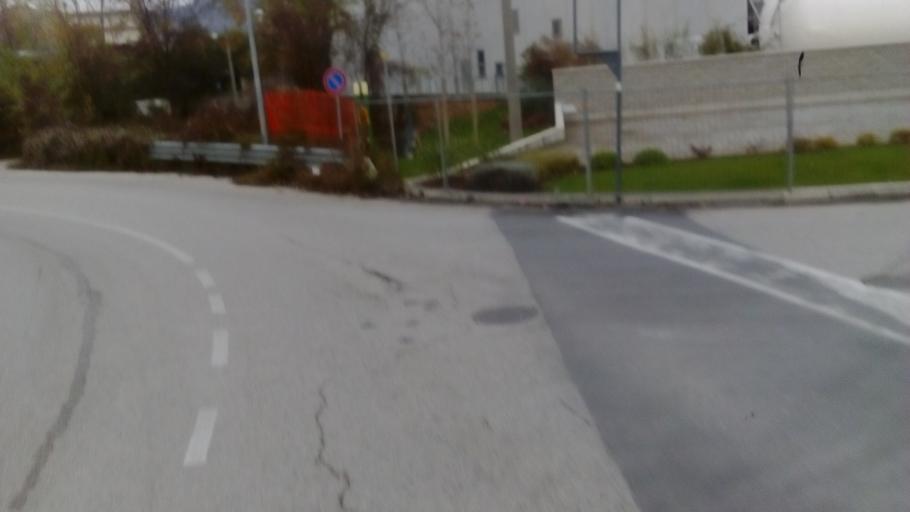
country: IT
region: Veneto
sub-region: Provincia di Vicenza
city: Chiampo
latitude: 45.5329
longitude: 11.3005
